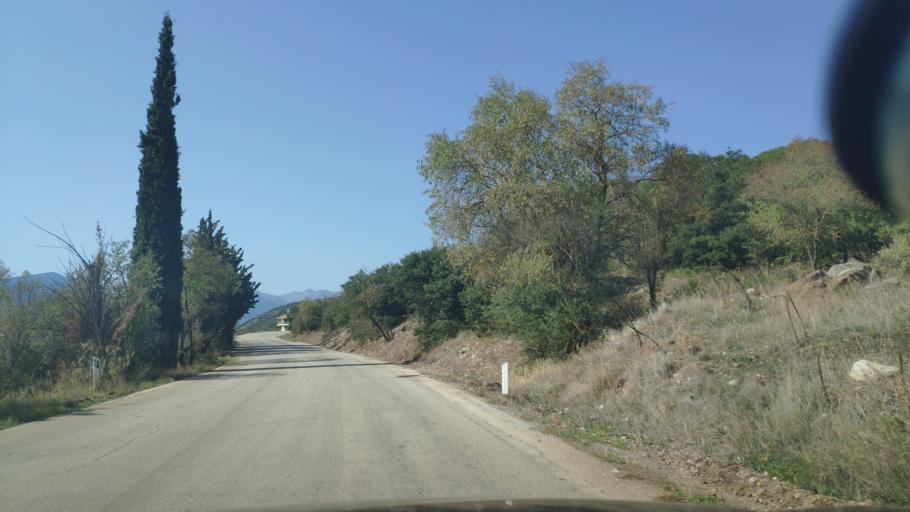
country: GR
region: Peloponnese
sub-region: Nomos Korinthias
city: Nemea
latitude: 37.8913
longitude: 22.5155
